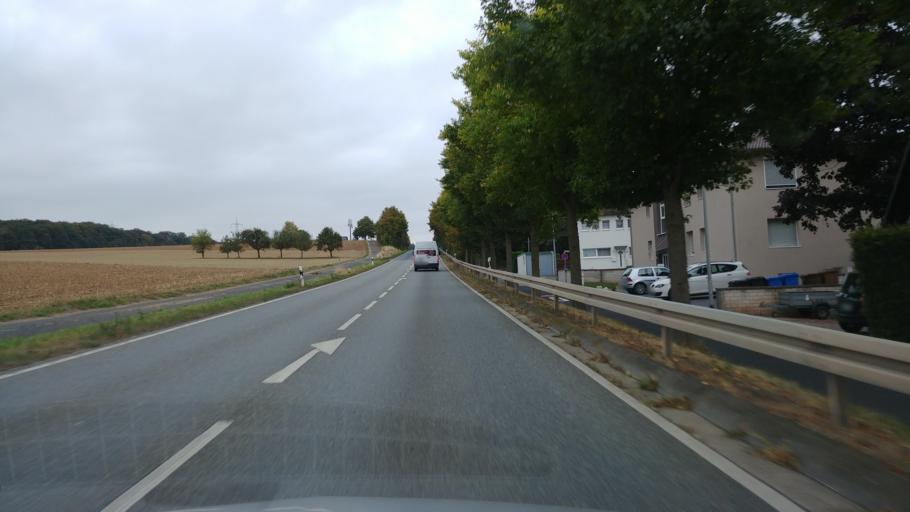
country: DE
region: Rheinland-Pfalz
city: Kaltenholzhausen
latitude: 50.3046
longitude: 8.1630
